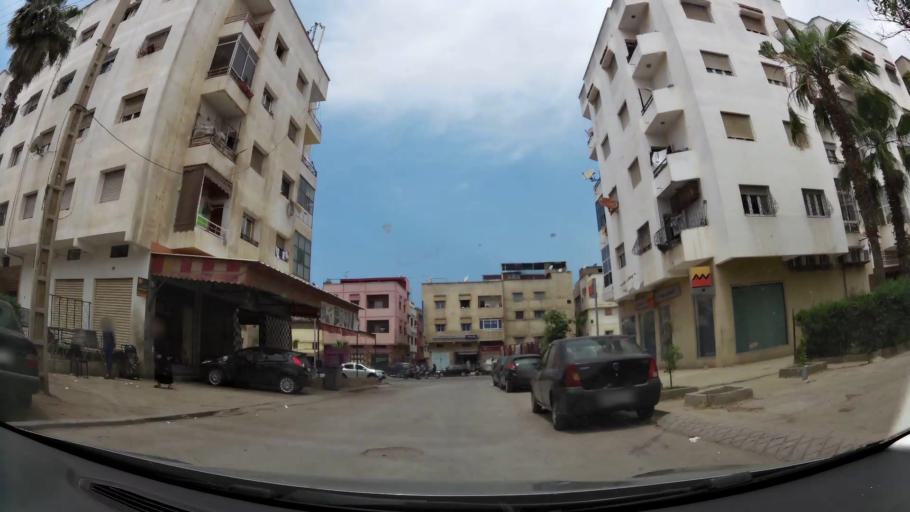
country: MA
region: Rabat-Sale-Zemmour-Zaer
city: Sale
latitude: 34.0590
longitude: -6.7849
